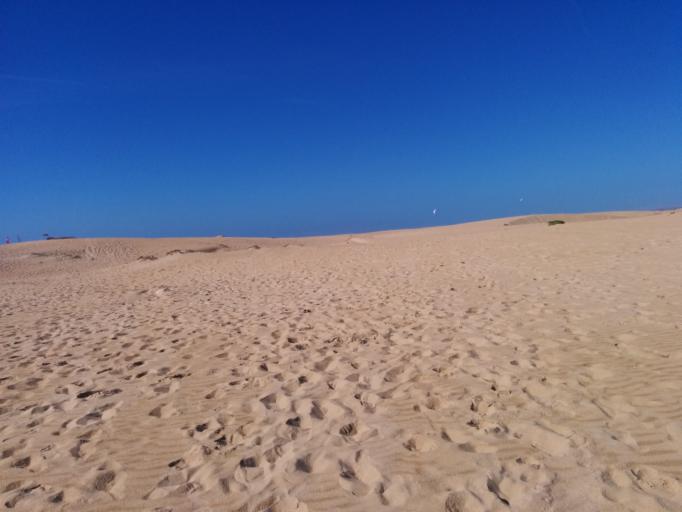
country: PT
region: Faro
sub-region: Vila do Bispo
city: Vila do Bispo
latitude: 37.1960
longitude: -8.9019
